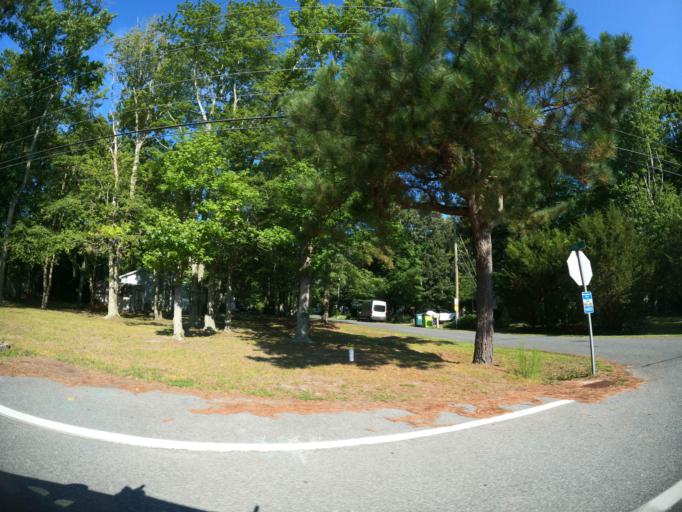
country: US
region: Delaware
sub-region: Sussex County
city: Ocean View
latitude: 38.5284
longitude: -75.0923
